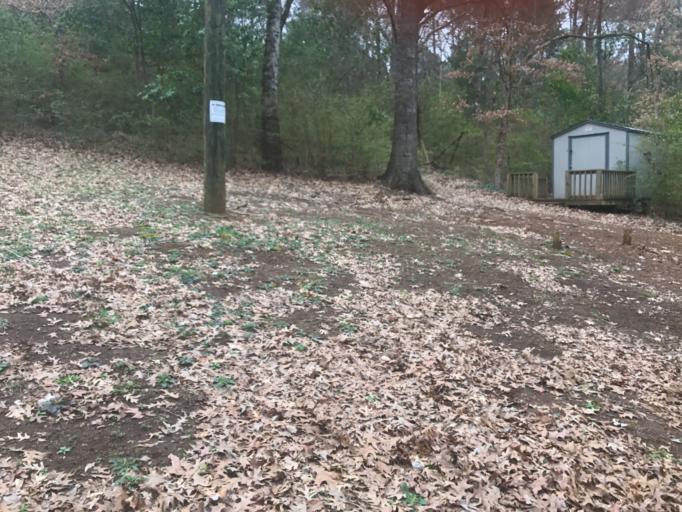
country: US
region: Texas
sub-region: Nacogdoches County
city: Nacogdoches
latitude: 31.6258
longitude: -94.6395
